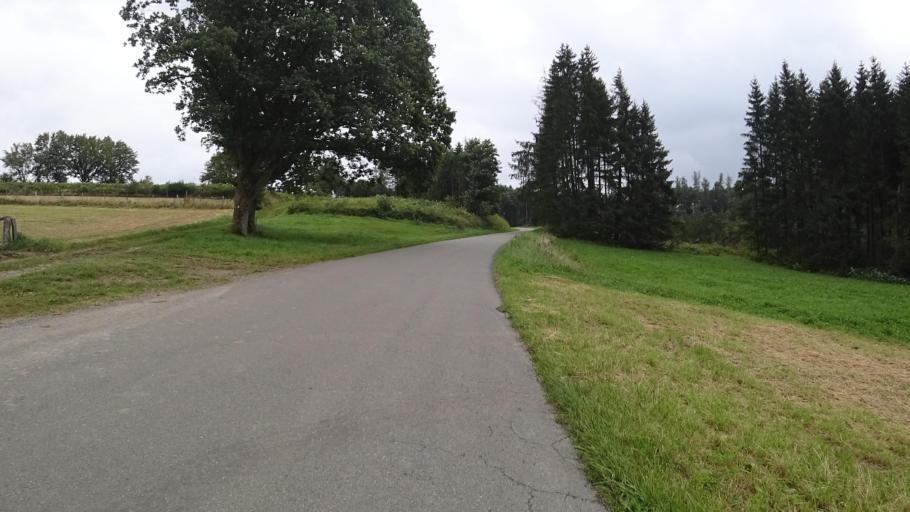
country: BE
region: Wallonia
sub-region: Province du Luxembourg
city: Chiny
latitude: 49.8020
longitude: 5.3722
